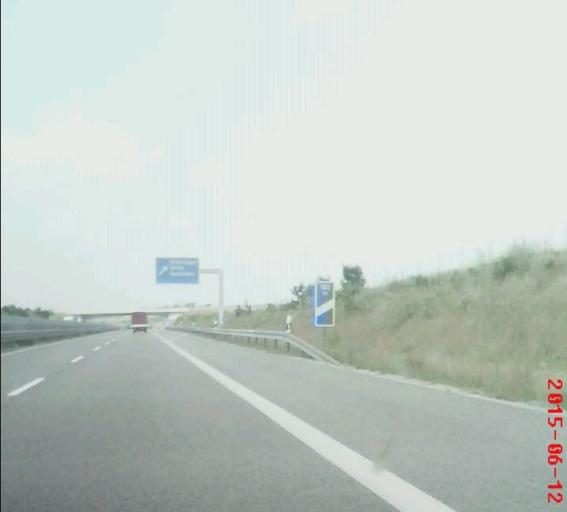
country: DE
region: Thuringia
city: Heldrungen
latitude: 51.3024
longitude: 11.2376
